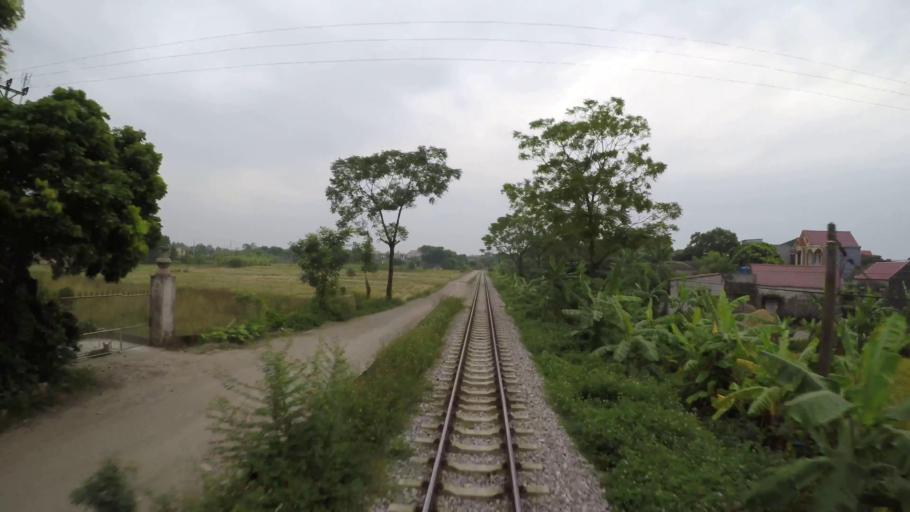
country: VN
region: Hai Duong
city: Ke Sat
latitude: 20.9661
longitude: 106.1378
